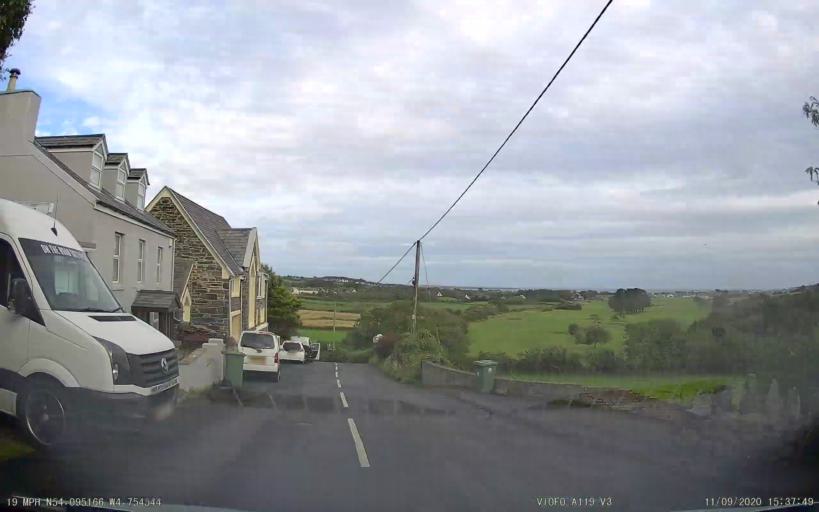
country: IM
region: Port Erin
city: Port Erin
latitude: 54.0952
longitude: -4.7546
